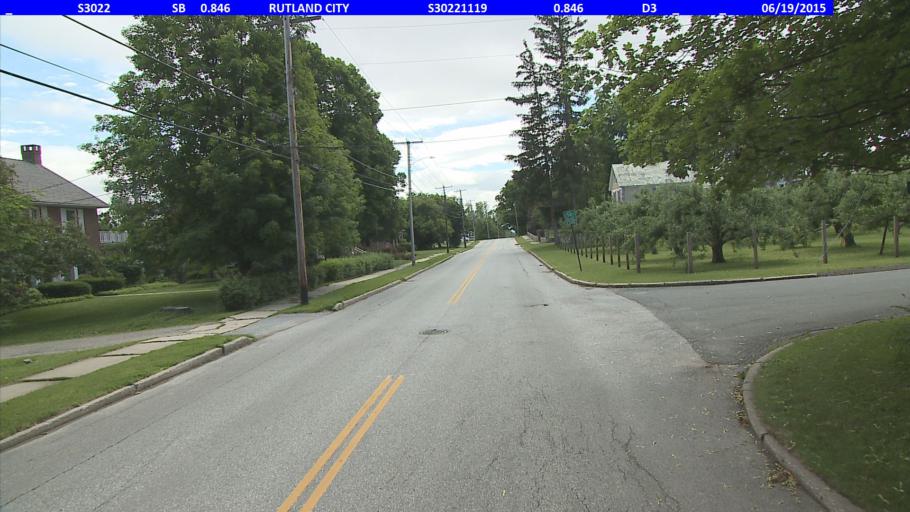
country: US
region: Vermont
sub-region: Rutland County
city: Rutland
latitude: 43.6208
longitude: -72.9850
